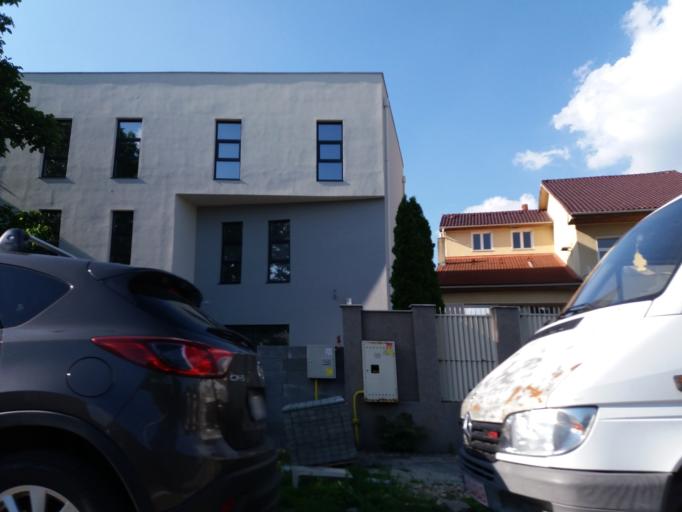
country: RO
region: Arad
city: Arad
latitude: 46.1693
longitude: 21.2978
